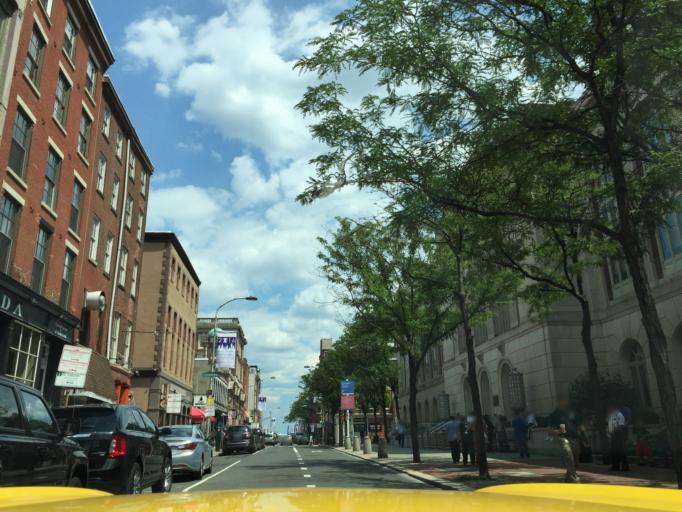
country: US
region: Pennsylvania
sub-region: Philadelphia County
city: Philadelphia
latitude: 39.9485
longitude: -75.1451
